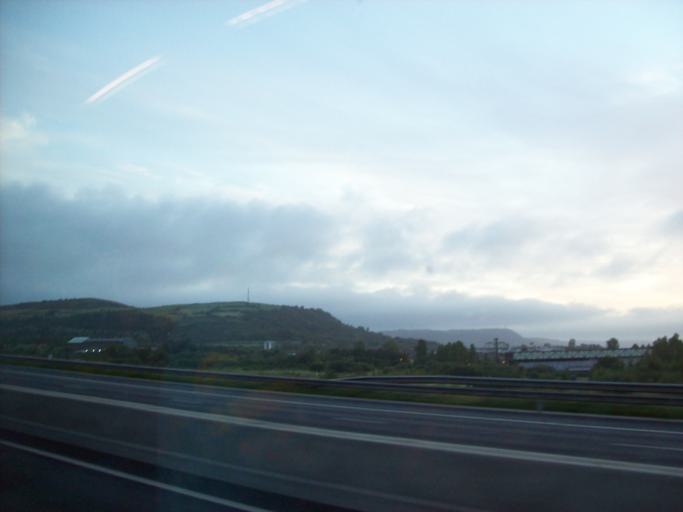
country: GB
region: Northern Ireland
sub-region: Newtownabbey District
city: Newtownabbey
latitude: 54.6542
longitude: -5.9301
